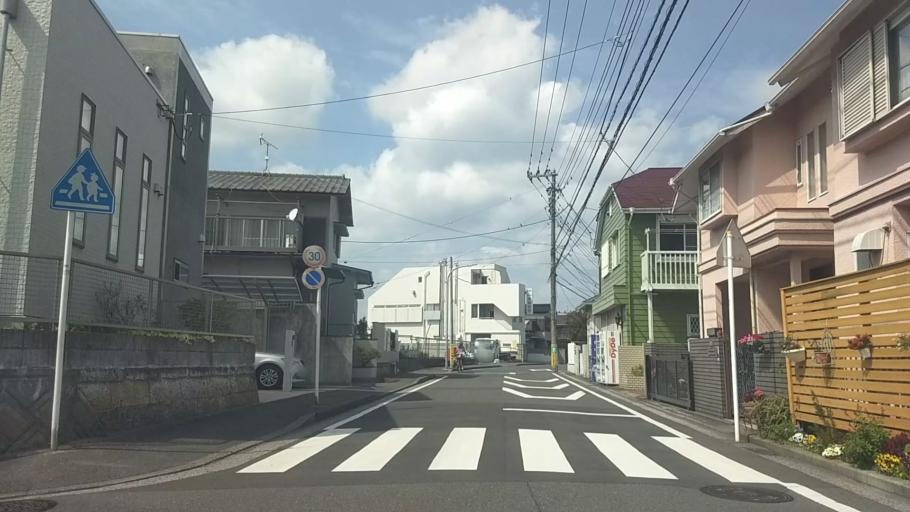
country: JP
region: Kanagawa
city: Kamakura
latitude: 35.3779
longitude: 139.5737
